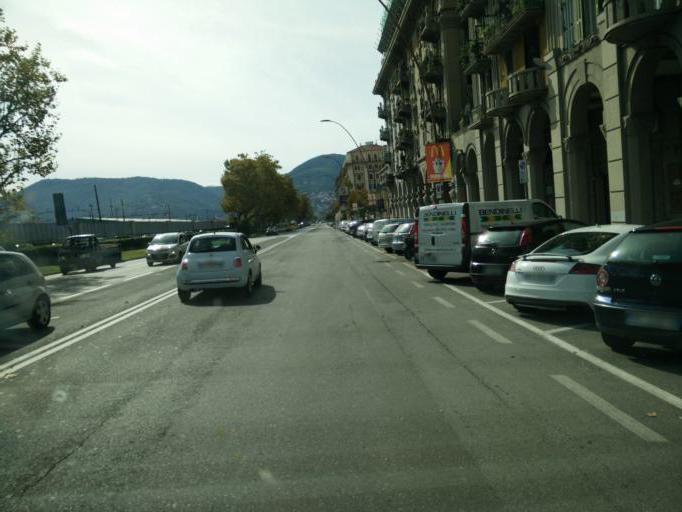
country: IT
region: Liguria
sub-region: Provincia di La Spezia
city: La Spezia
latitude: 44.1102
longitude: 9.8336
